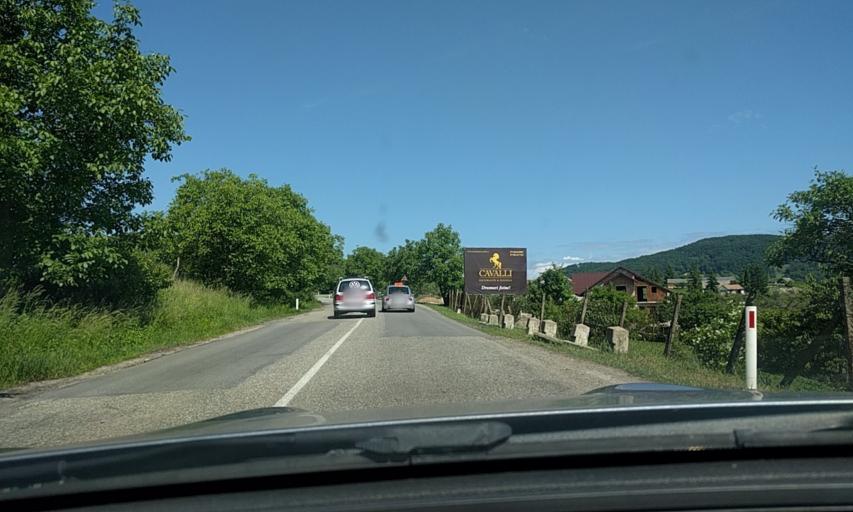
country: RO
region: Bistrita-Nasaud
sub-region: Municipiul Bistrita
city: Unirea
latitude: 47.1717
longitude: 24.4963
